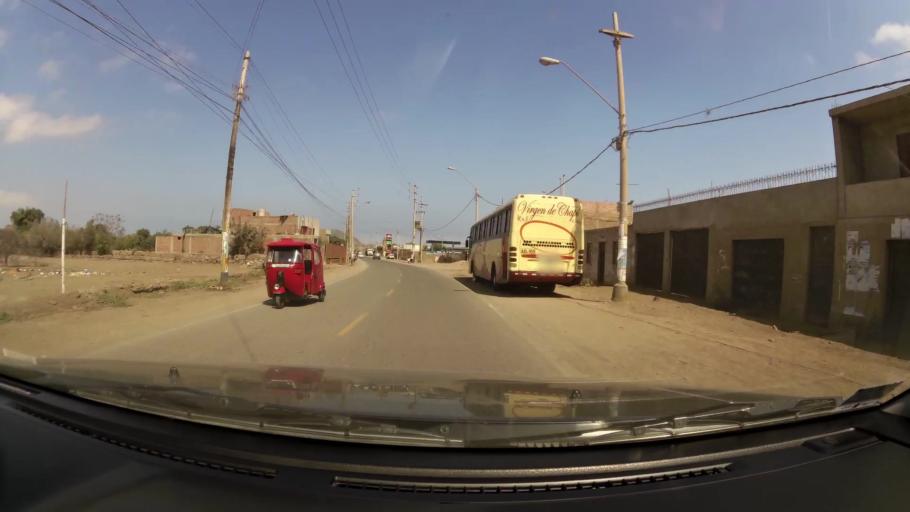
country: PE
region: Lima
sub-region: Provincia de Canete
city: Mala
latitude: -12.6645
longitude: -76.6403
